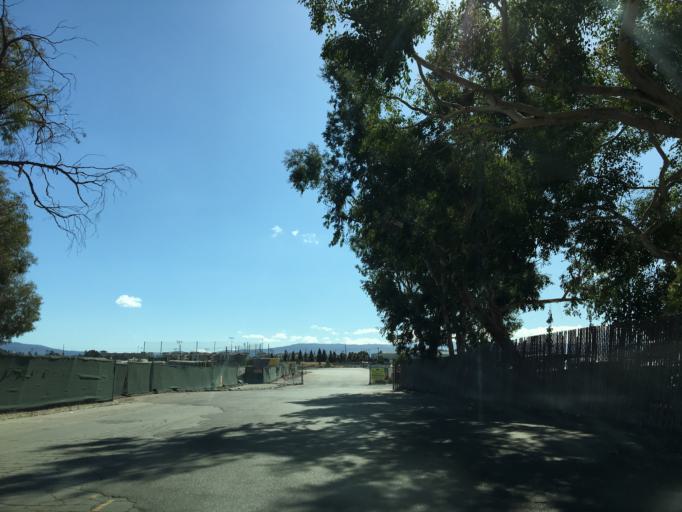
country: US
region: California
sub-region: Santa Clara County
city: Santa Clara
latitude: 37.3544
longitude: -121.9288
